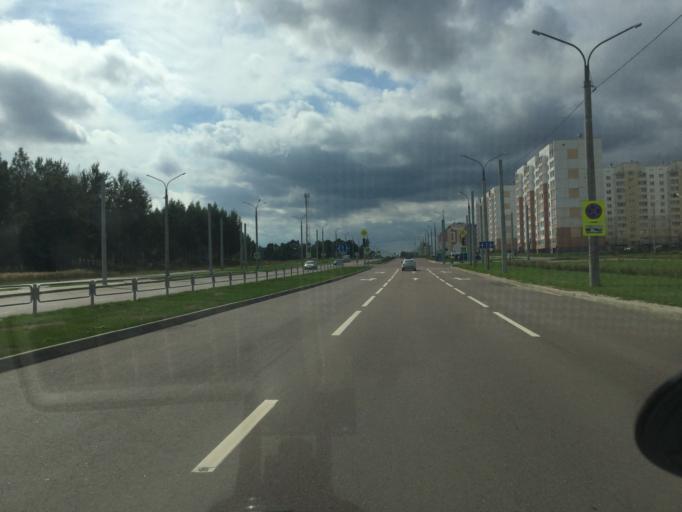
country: BY
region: Vitebsk
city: Vitebsk
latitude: 55.1675
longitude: 30.2931
